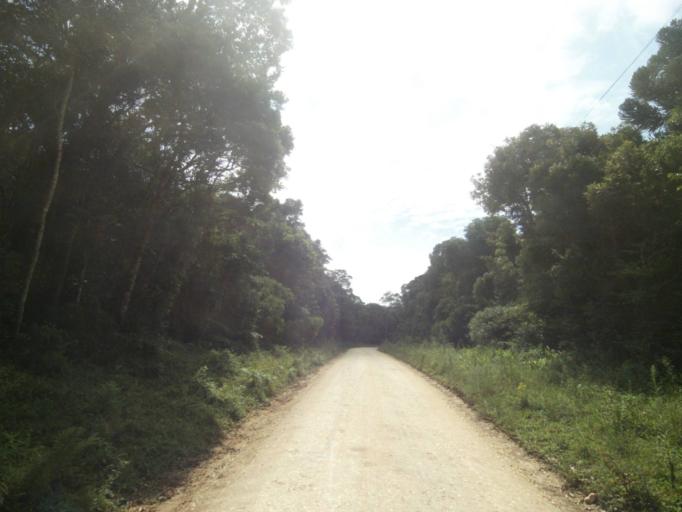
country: BR
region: Parana
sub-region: Campina Grande Do Sul
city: Campina Grande do Sul
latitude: -25.3221
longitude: -49.0682
